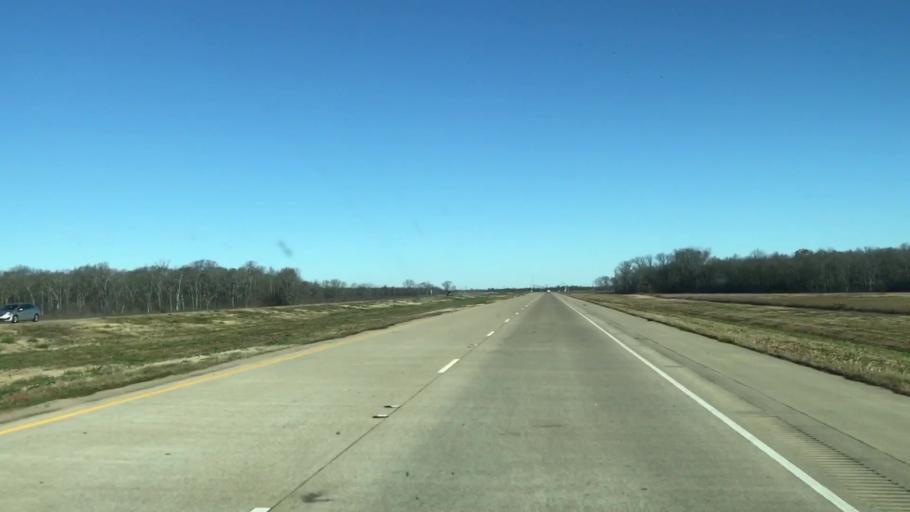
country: US
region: Louisiana
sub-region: Caddo Parish
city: Blanchard
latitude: 32.6399
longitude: -93.8382
